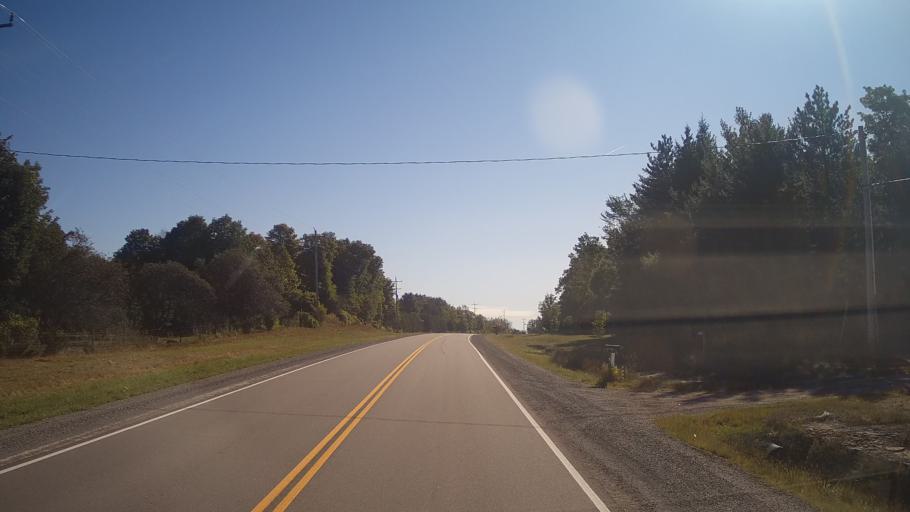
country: CA
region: Ontario
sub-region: Lanark County
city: Smiths Falls
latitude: 44.6253
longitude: -75.9864
